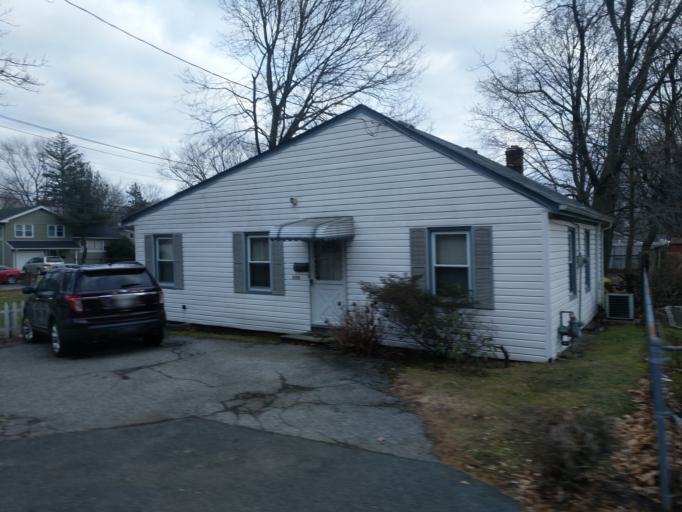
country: US
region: New York
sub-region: Nassau County
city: East Garden City
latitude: 40.7207
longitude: -73.6091
